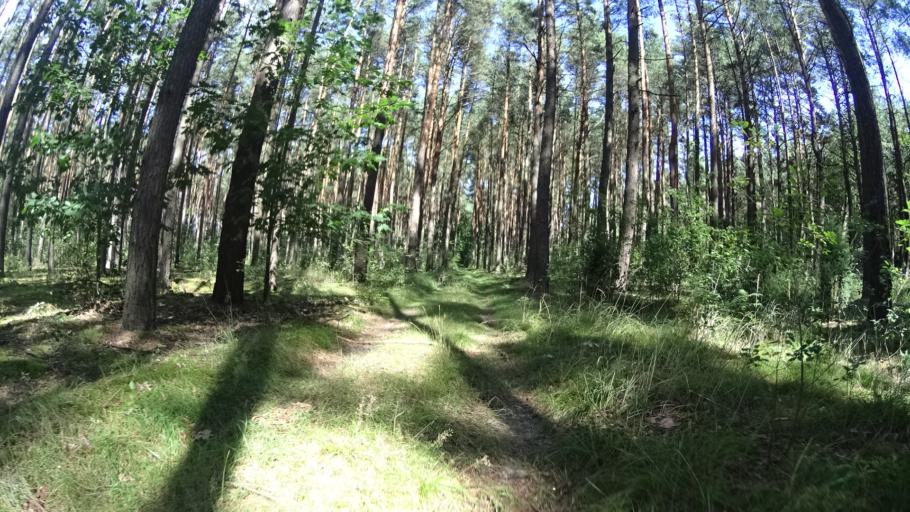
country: PL
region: Masovian Voivodeship
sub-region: Powiat grojecki
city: Mogielnica
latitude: 51.6750
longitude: 20.7498
